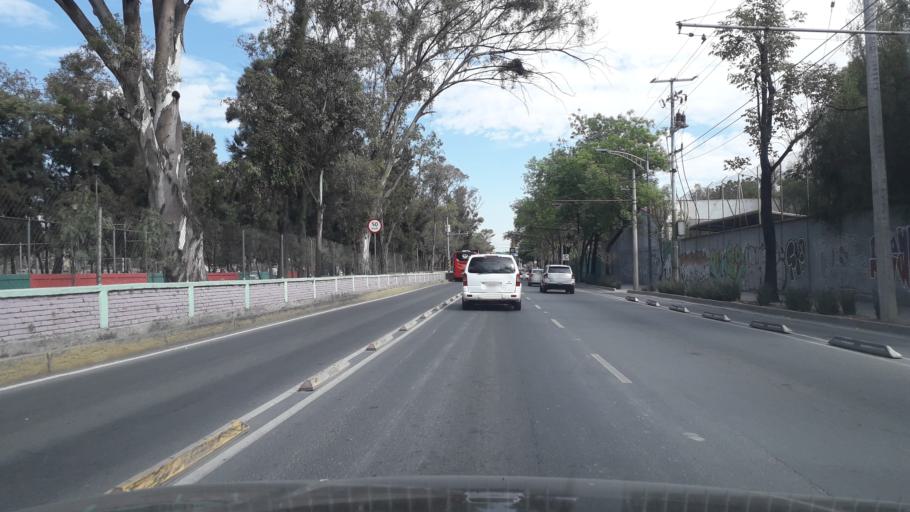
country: MX
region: Mexico City
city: Gustavo A. Madero
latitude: 19.4768
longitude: -99.0985
